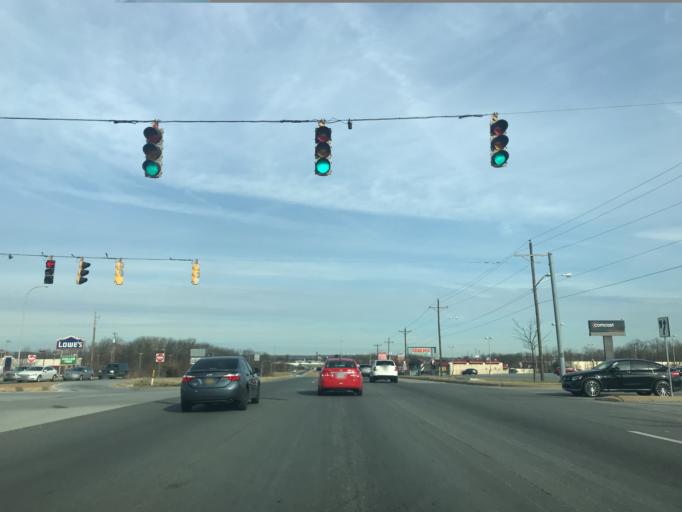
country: US
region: Delaware
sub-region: New Castle County
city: Wilmington Manor
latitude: 39.7108
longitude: -75.5628
